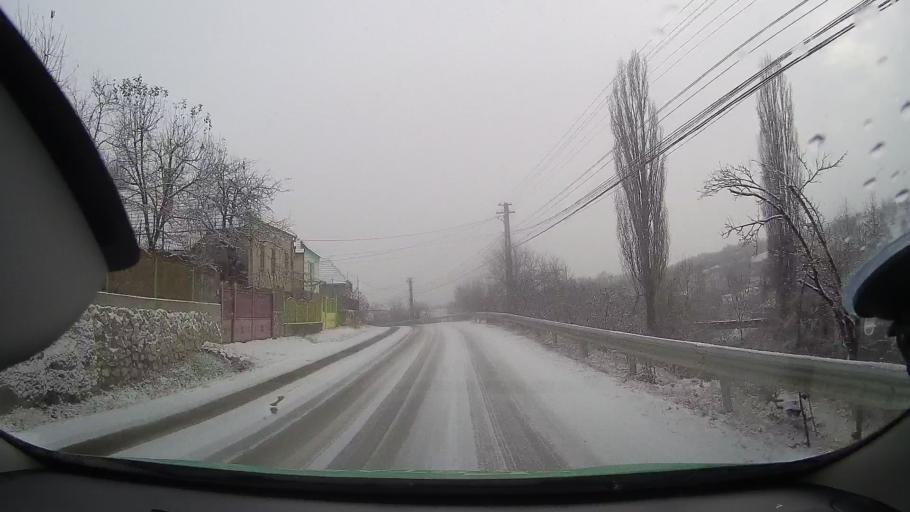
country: RO
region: Alba
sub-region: Comuna Livezile
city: Livezile
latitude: 46.3481
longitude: 23.6384
